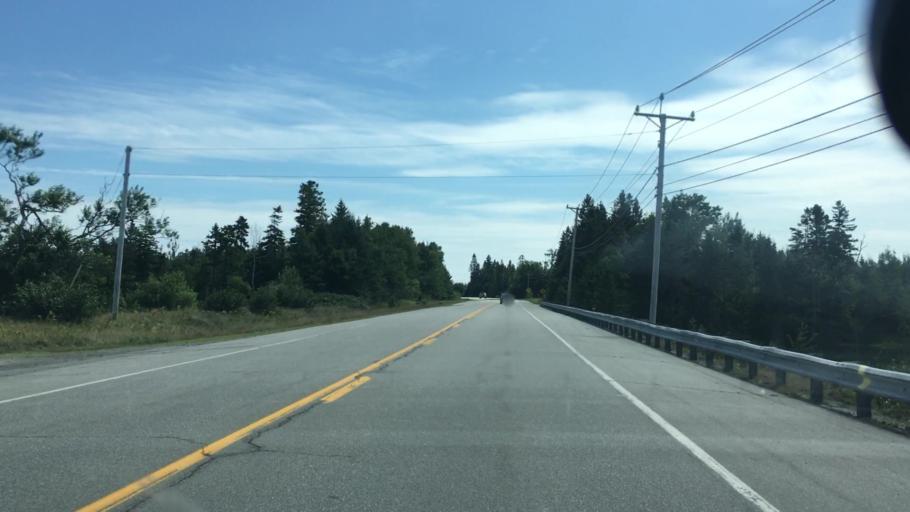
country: US
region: Maine
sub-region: Washington County
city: Eastport
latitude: 44.9458
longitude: -67.0393
